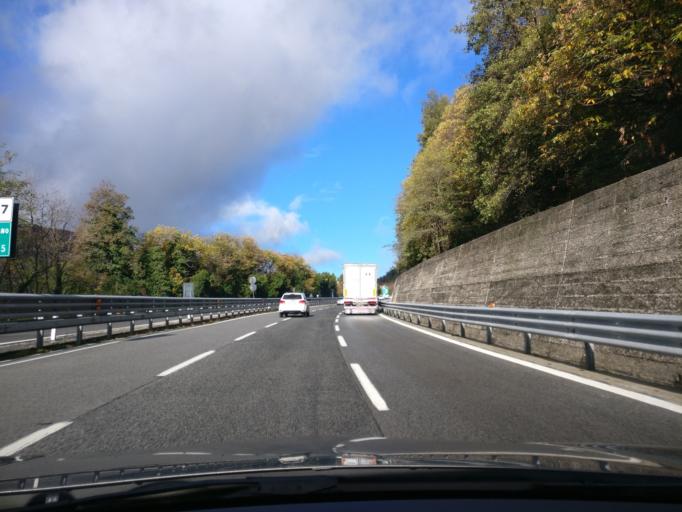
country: IT
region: Campania
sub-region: Provincia di Avellino
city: Monteforte Irpino
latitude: 40.8965
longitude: 14.7163
